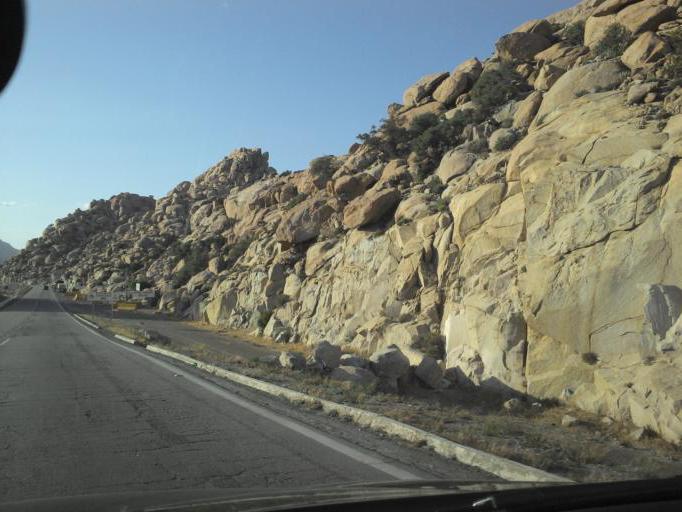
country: MX
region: Baja California
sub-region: Tecate
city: Cereso del Hongo
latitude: 32.5595
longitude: -116.0357
